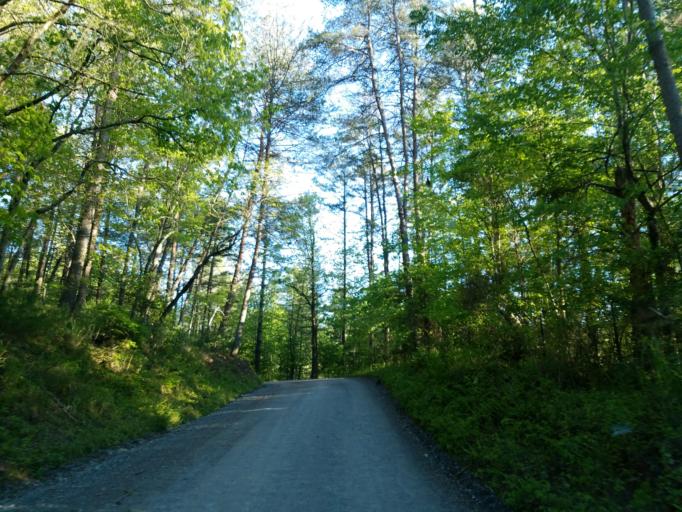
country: US
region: Georgia
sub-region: Fannin County
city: Blue Ridge
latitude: 34.7573
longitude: -84.1939
